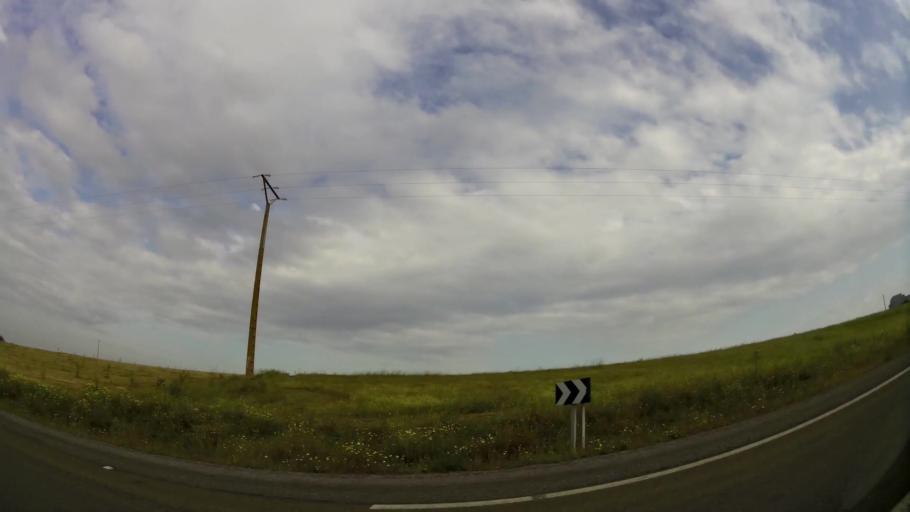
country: MA
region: Rabat-Sale-Zemmour-Zaer
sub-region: Khemisset
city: Khemisset
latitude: 33.7918
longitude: -6.1160
